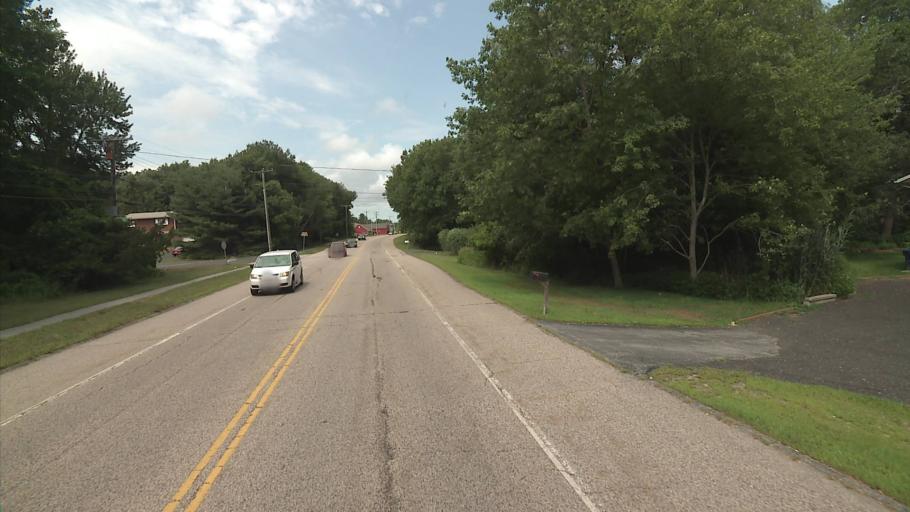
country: US
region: Connecticut
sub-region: New London County
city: Central Waterford
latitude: 41.3300
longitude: -72.1354
